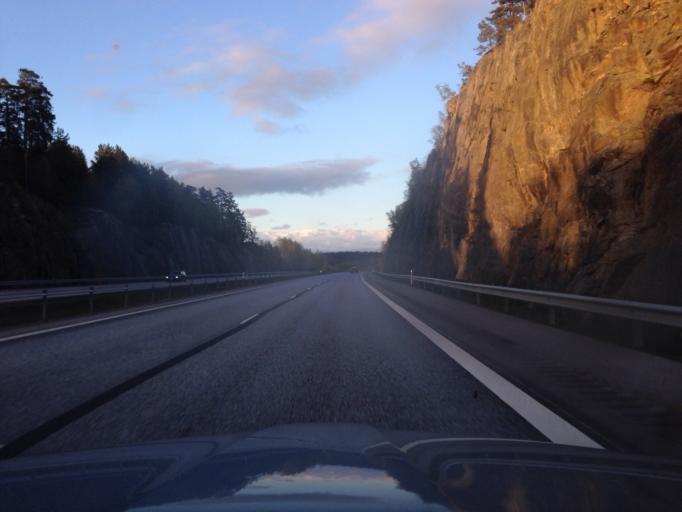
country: SE
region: Soedermanland
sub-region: Trosa Kommun
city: Vagnharad
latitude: 58.9320
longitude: 17.4085
